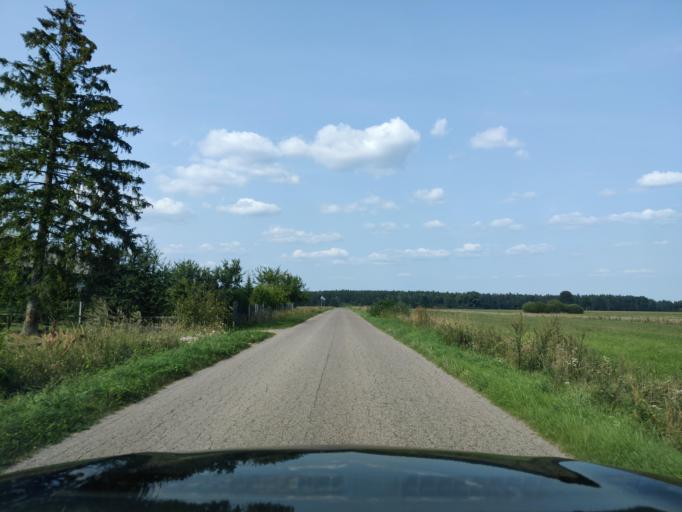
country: PL
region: Masovian Voivodeship
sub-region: Powiat wyszkowski
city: Rzasnik
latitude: 52.7449
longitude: 21.3183
